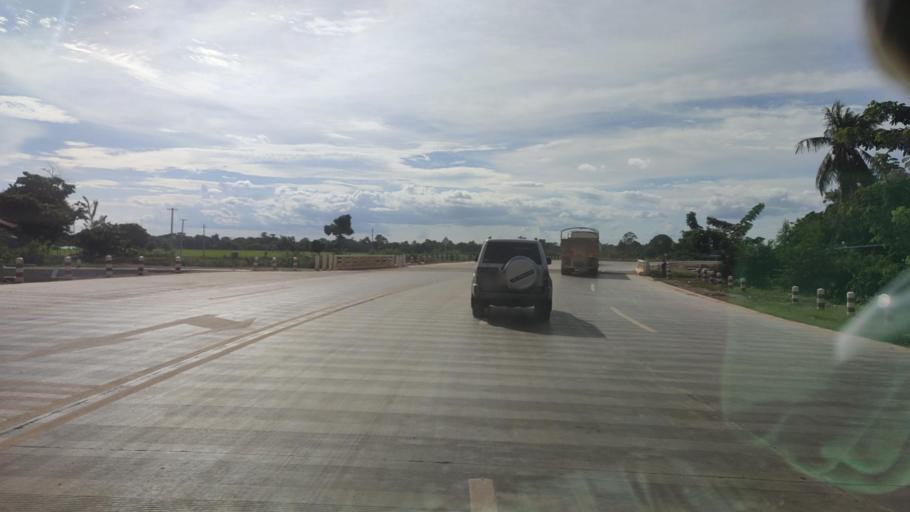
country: MM
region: Mandalay
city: Kyaukse
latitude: 21.6218
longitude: 96.1386
